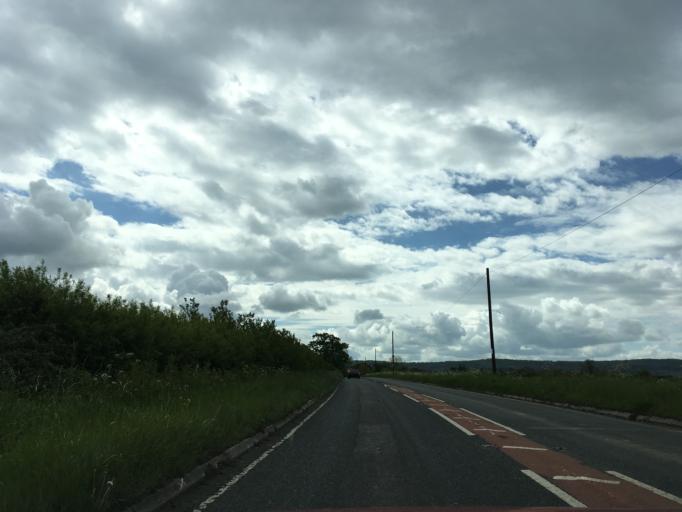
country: GB
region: England
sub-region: Gloucestershire
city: Stonehouse
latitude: 51.7593
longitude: -2.2843
